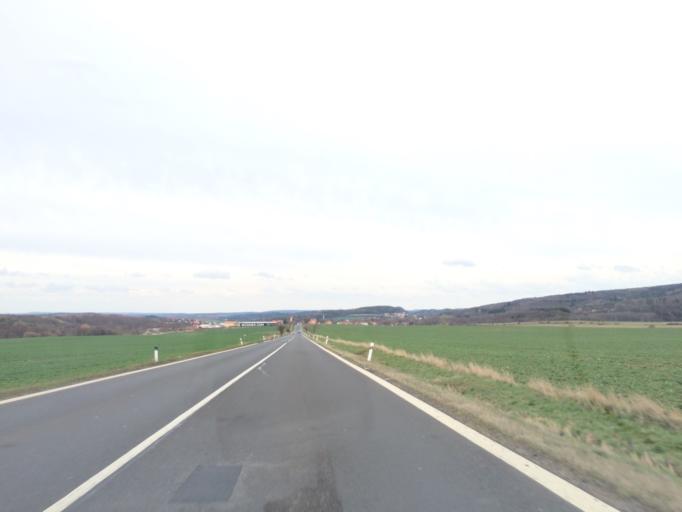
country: CZ
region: Ustecky
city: Lubenec
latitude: 50.1324
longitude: 13.2907
